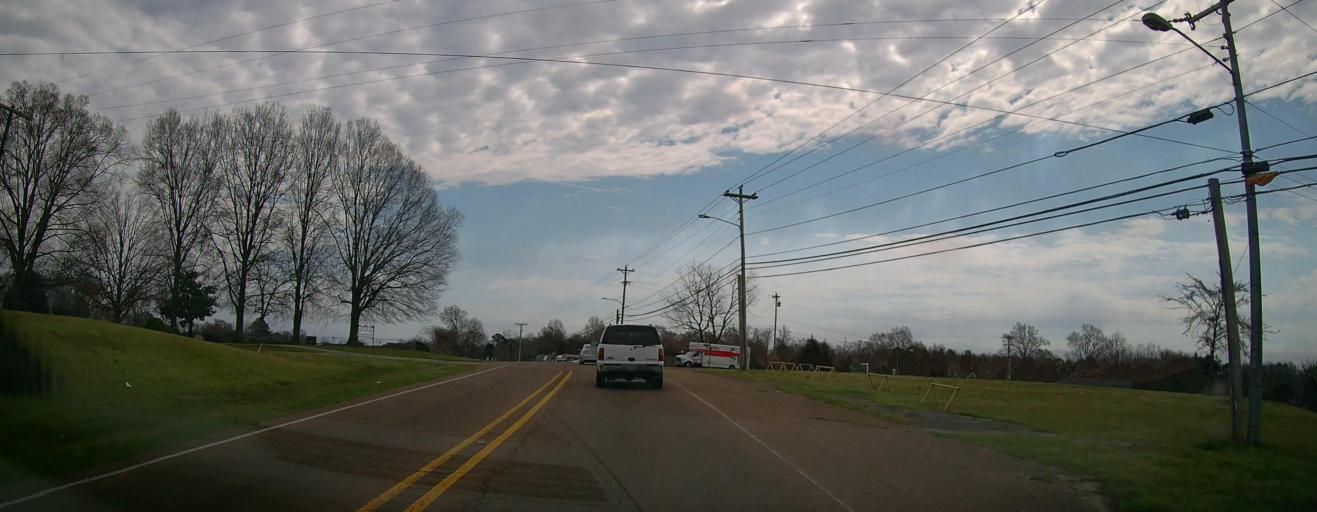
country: US
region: Mississippi
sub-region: Marshall County
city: Byhalia
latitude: 34.8732
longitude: -89.6977
